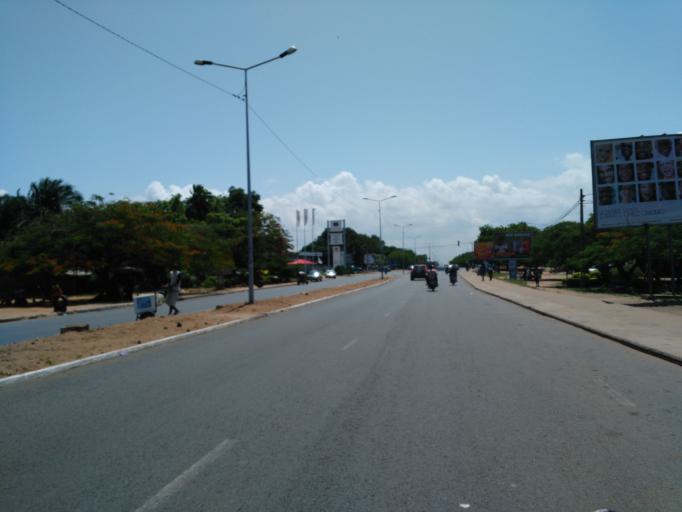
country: TG
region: Maritime
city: Lome
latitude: 6.1546
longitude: 1.2281
